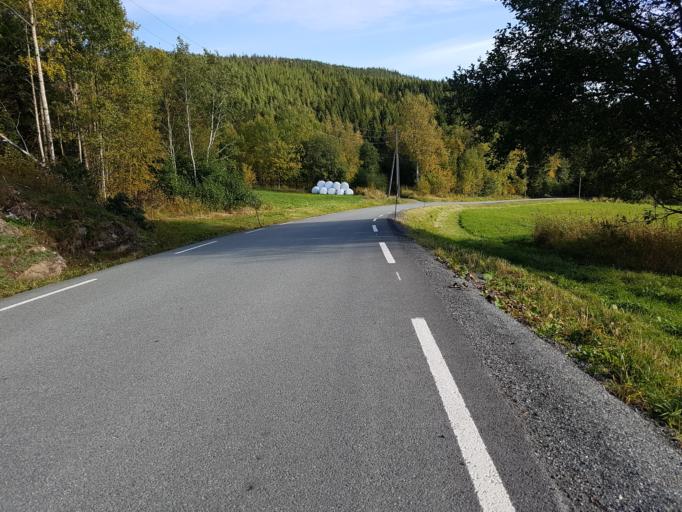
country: NO
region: Sor-Trondelag
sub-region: Malvik
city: Malvik
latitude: 63.3638
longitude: 10.6250
